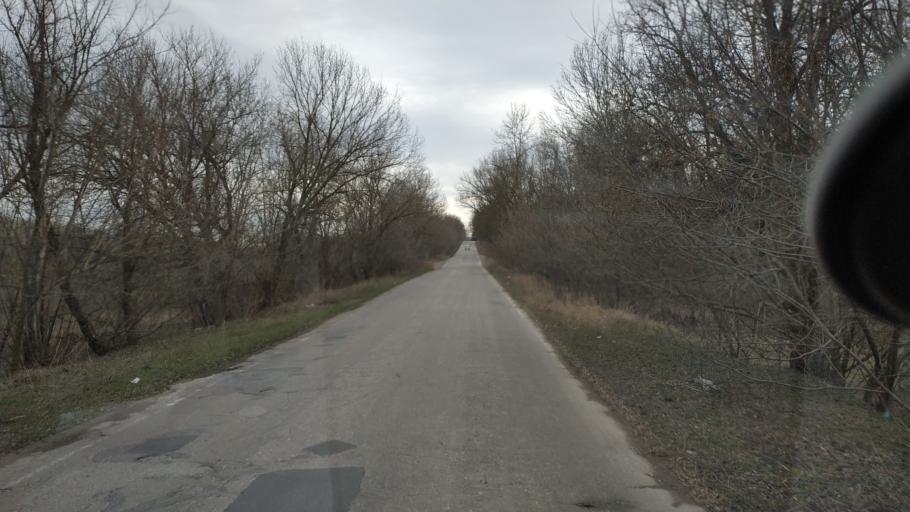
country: MD
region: Chisinau
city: Vadul lui Voda
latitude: 47.1069
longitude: 29.0635
